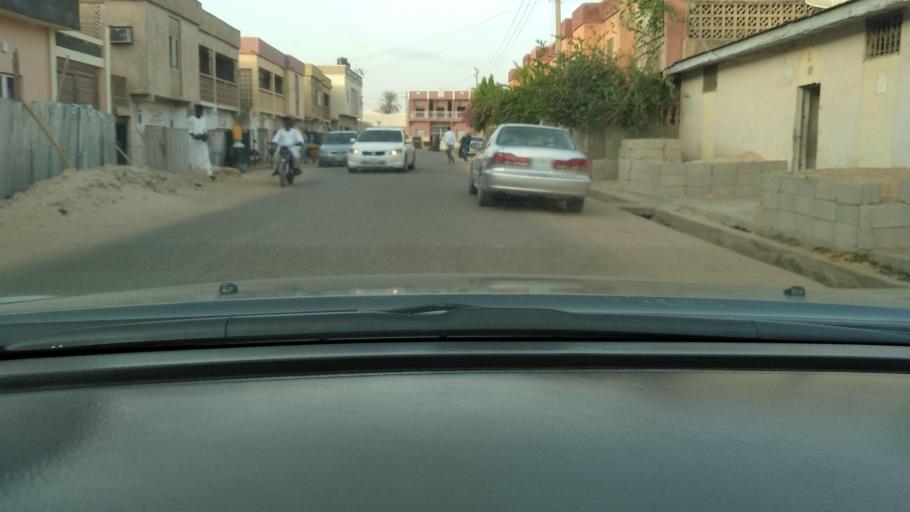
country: NG
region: Kano
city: Kano
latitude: 11.9598
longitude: 8.5250
